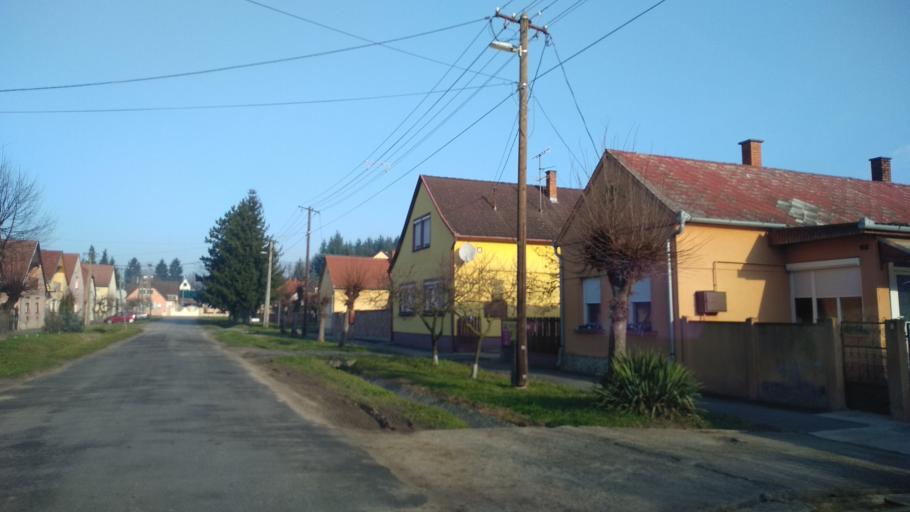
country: HU
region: Somogy
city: Barcs
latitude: 45.9650
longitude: 17.4744
